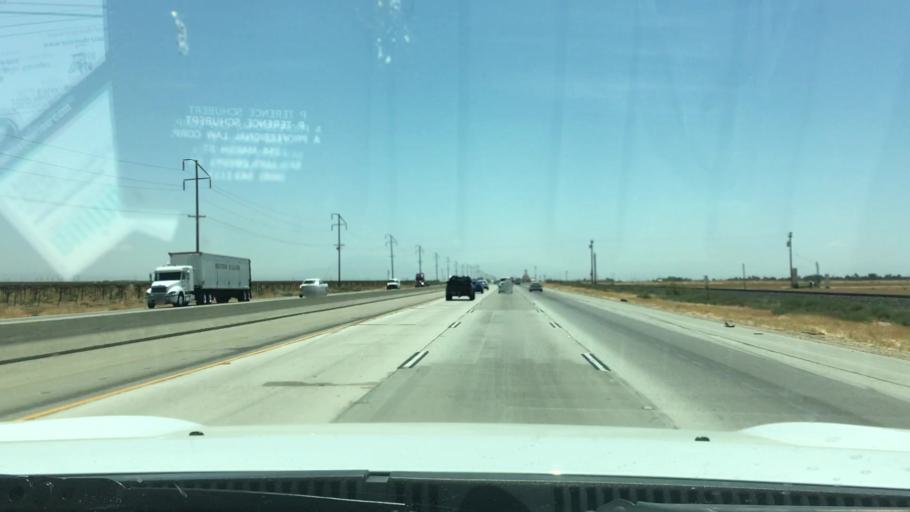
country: US
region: California
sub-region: Kern County
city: Greenacres
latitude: 35.4672
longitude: -119.1214
